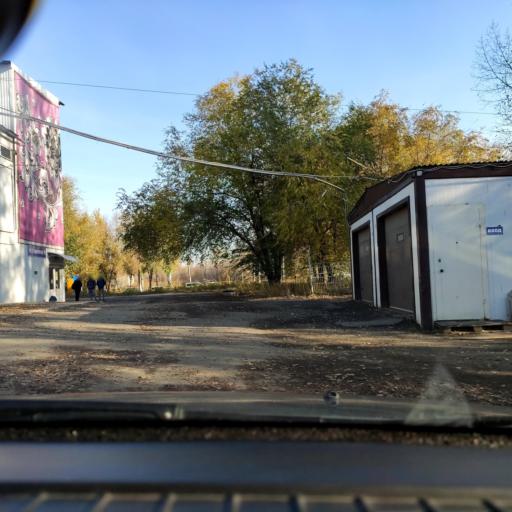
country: RU
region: Samara
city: Tol'yatti
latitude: 53.5384
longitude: 49.2771
